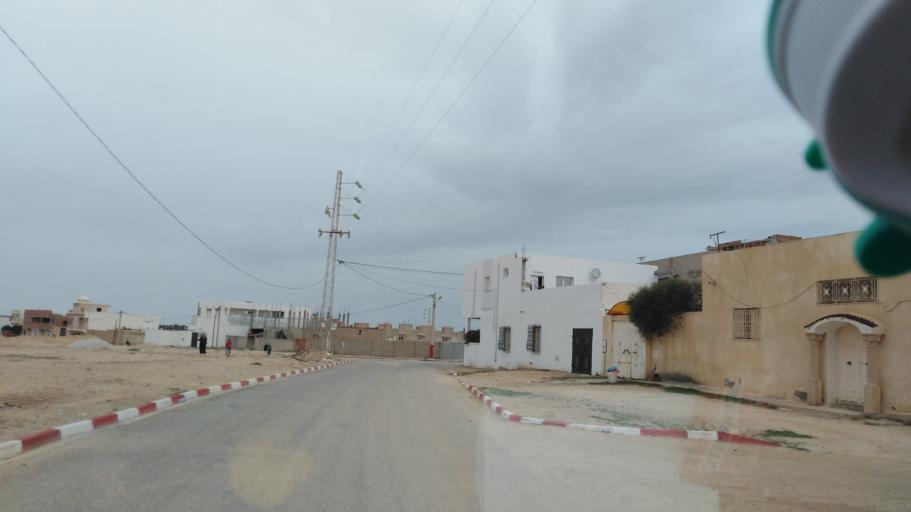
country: TN
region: Qabis
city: Gabes
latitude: 33.9524
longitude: 10.0031
